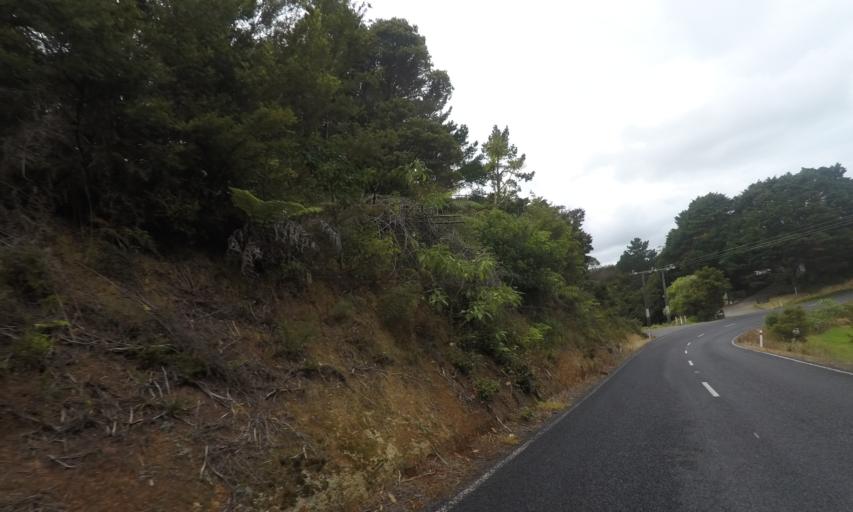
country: NZ
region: Northland
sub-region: Whangarei
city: Whangarei
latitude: -35.7587
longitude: 174.4547
